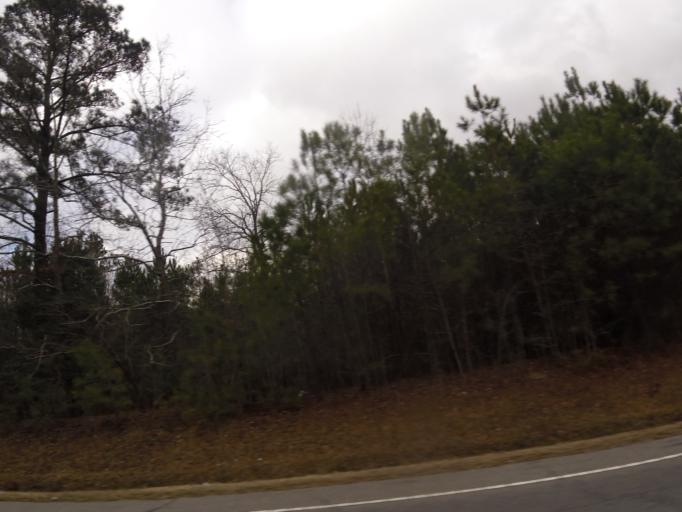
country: US
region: North Carolina
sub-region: Edgecombe County
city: Pinetops
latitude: 35.8563
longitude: -77.6861
